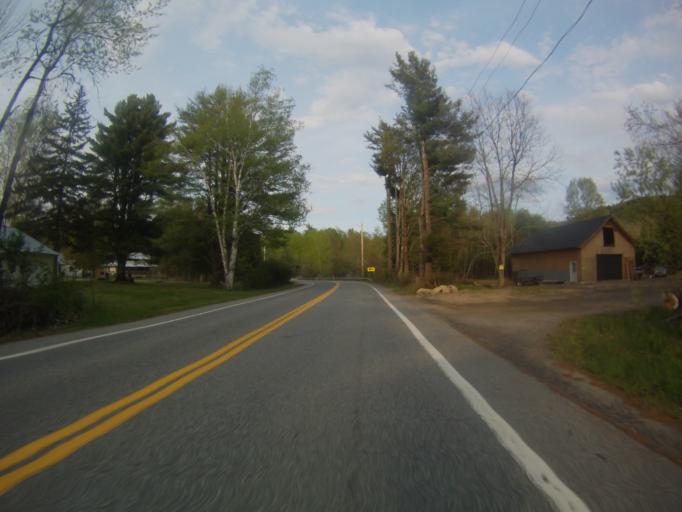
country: US
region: New York
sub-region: Essex County
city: Ticonderoga
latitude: 43.7546
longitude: -73.5547
